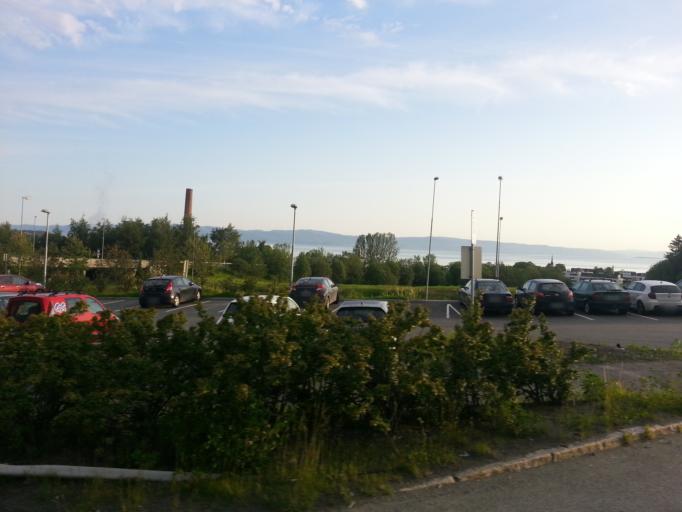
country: NO
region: Sor-Trondelag
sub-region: Klaebu
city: Klaebu
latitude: 63.4215
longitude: 10.5352
